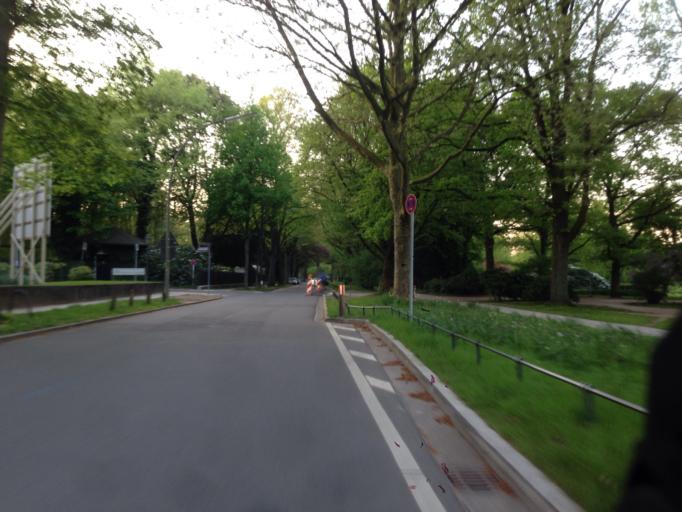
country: DE
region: Hamburg
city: Hamburg
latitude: 53.5704
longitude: 10.0003
